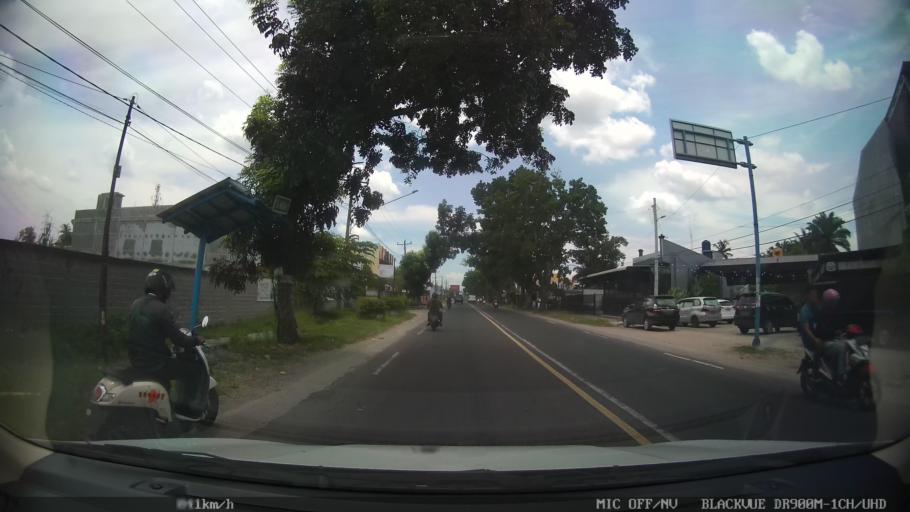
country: ID
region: North Sumatra
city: Binjai
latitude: 3.6236
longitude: 98.5045
